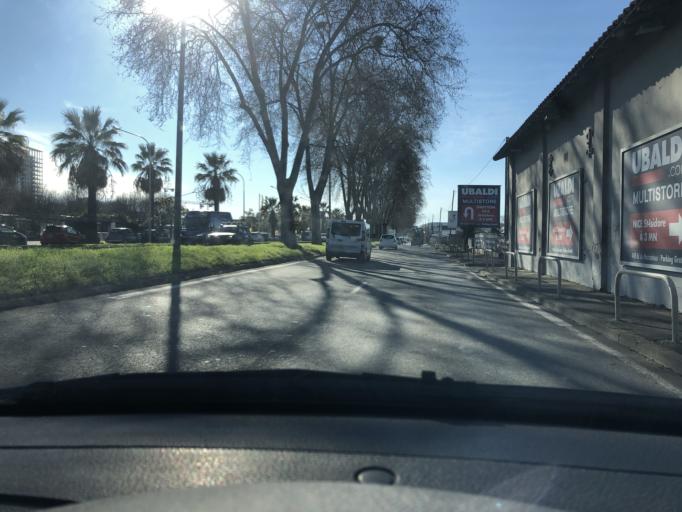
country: FR
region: Provence-Alpes-Cote d'Azur
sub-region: Departement des Alpes-Maritimes
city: Saint-Laurent-du-Var
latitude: 43.6850
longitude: 7.1979
